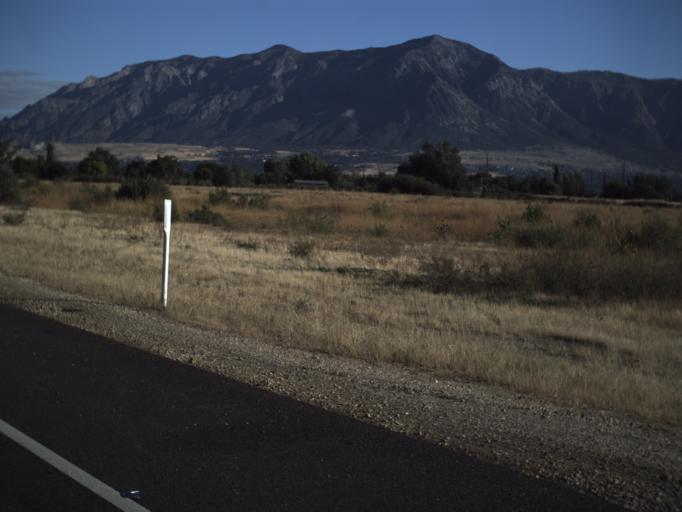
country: US
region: Utah
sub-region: Weber County
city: Marriott-Slaterville
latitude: 41.2452
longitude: -112.0153
